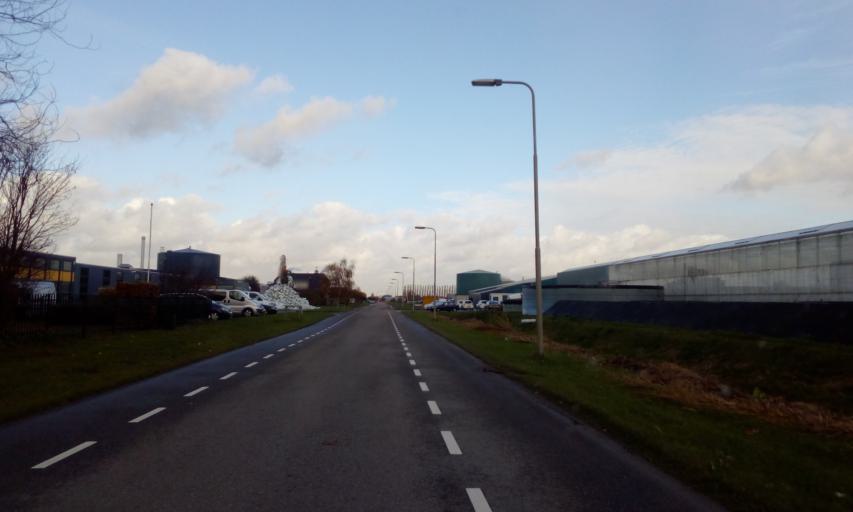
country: NL
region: South Holland
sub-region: Gemeente Lansingerland
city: Bleiswijk
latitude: 52.0119
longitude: 4.5158
